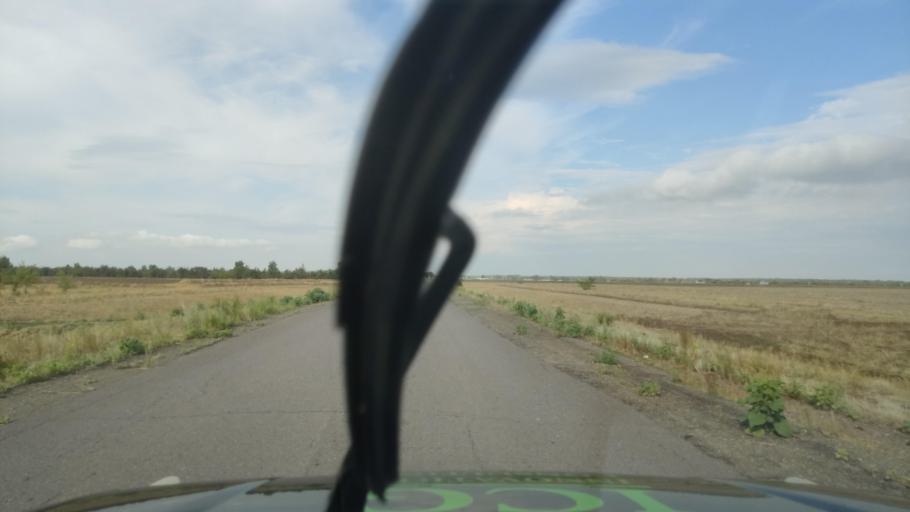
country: KZ
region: Pavlodar
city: Leninskiy
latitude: 52.4793
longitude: 76.8473
